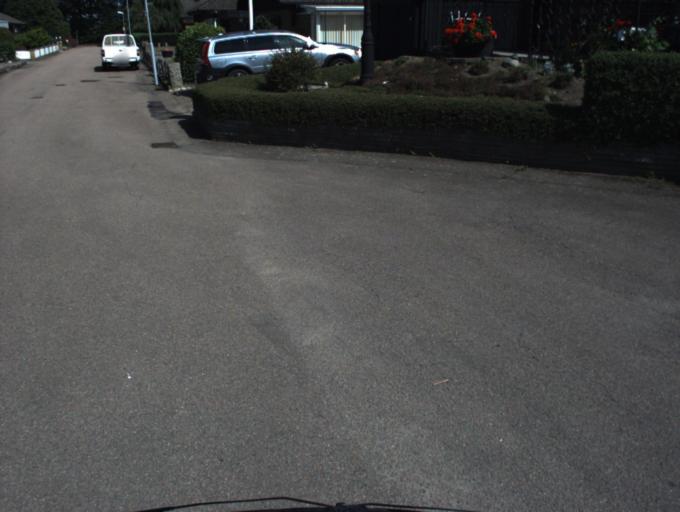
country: SE
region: Skane
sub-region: Helsingborg
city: Barslov
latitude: 56.0358
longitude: 12.8135
